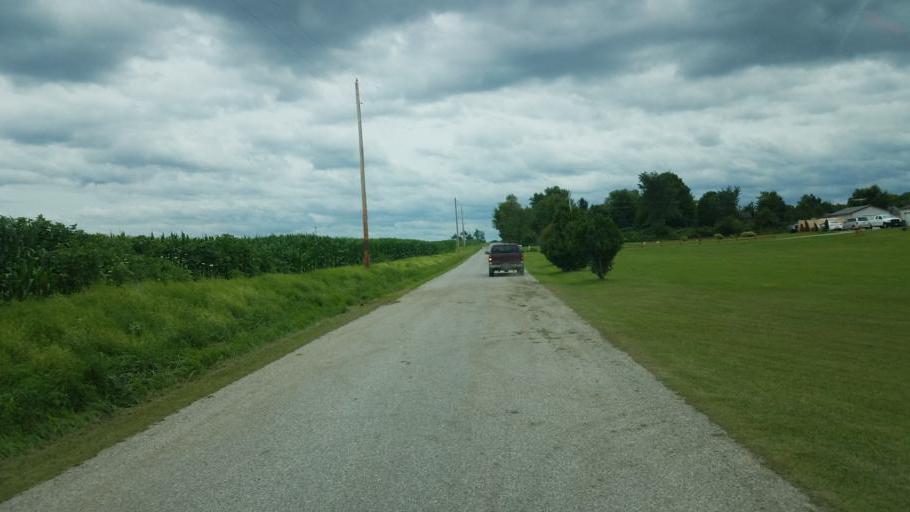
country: US
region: Ohio
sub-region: Licking County
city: Utica
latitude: 40.1931
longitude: -82.5504
